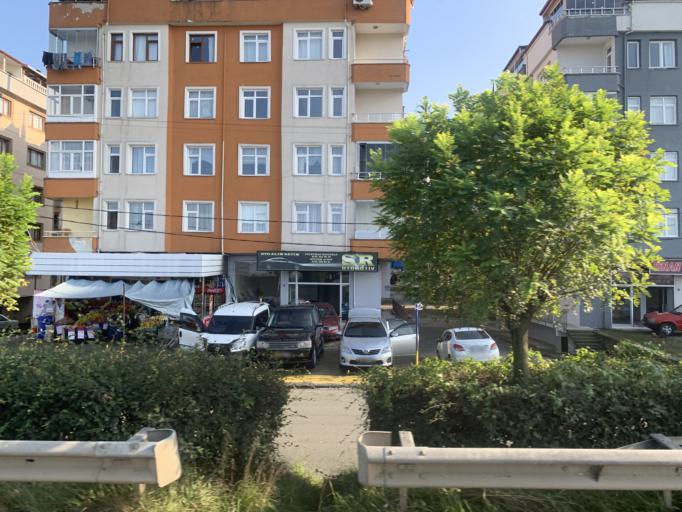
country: TR
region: Trabzon
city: Of
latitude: 40.9410
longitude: 40.2578
